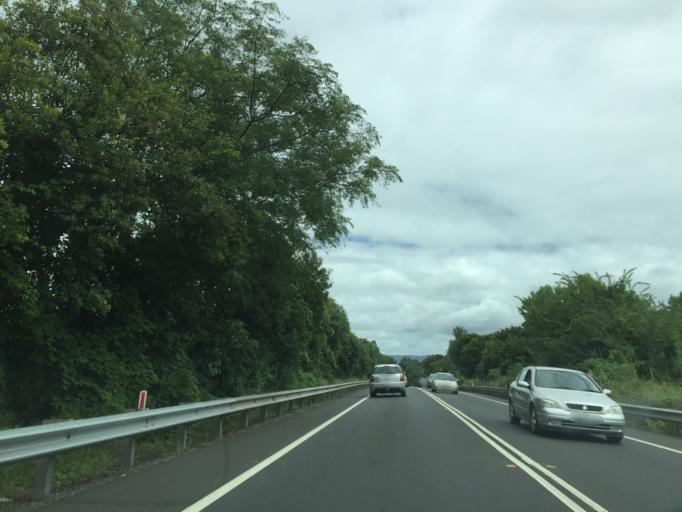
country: AU
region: New South Wales
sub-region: Hawkesbury
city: Richmond
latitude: -33.5883
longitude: 150.7287
